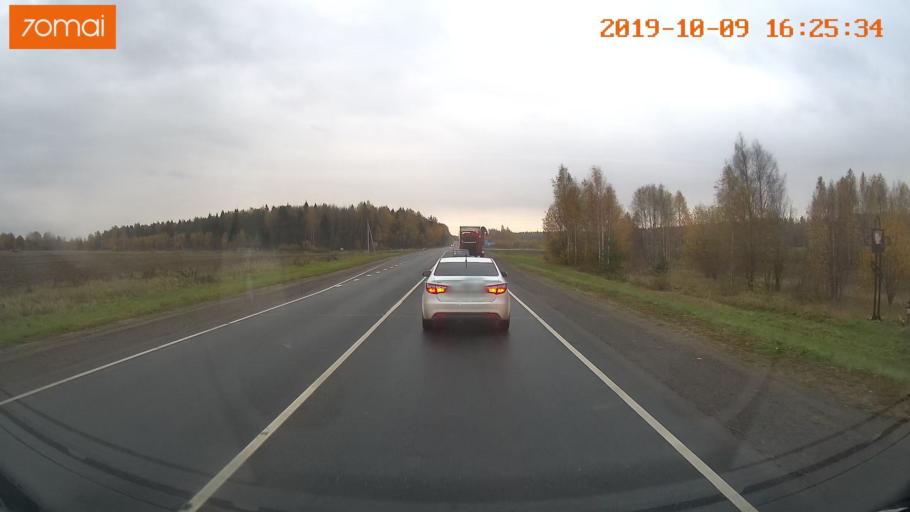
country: RU
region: Kostroma
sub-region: Kostromskoy Rayon
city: Kostroma
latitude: 57.6416
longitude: 40.9204
